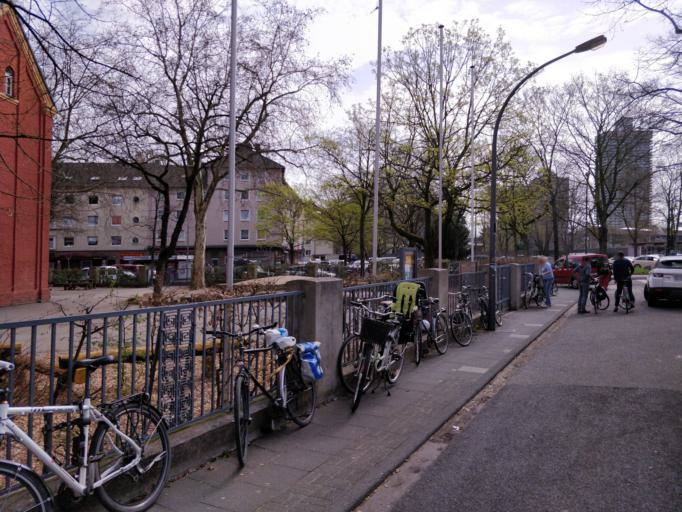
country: DE
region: North Rhine-Westphalia
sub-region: Regierungsbezirk Koln
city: Riehl
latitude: 50.9644
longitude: 6.9756
